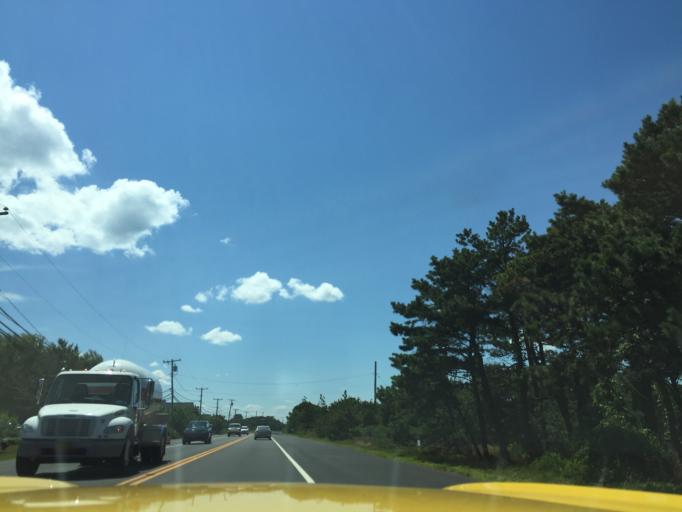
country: US
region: New York
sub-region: Suffolk County
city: Amagansett
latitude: 40.9959
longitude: -72.0537
